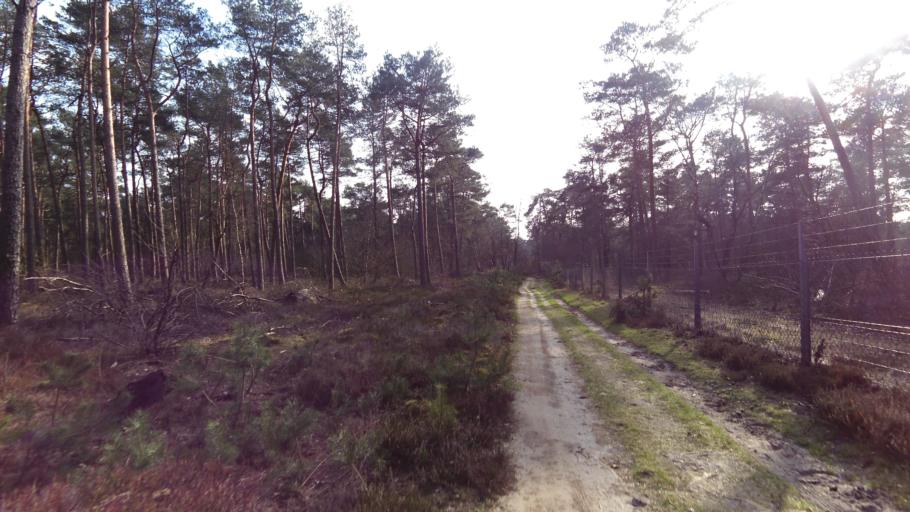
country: NL
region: Gelderland
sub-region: Gemeente Ede
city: Wekerom
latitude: 52.0842
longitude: 5.7358
